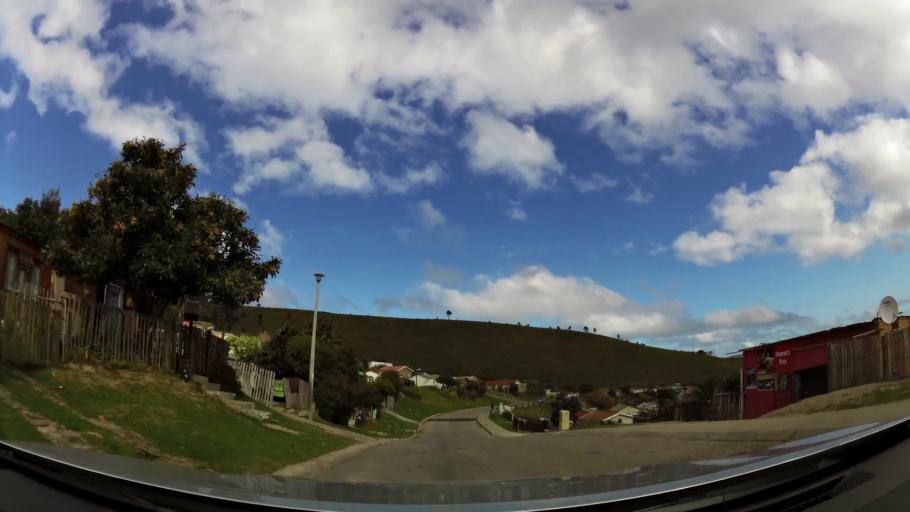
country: ZA
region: Western Cape
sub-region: Eden District Municipality
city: Knysna
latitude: -34.0531
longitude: 23.1053
